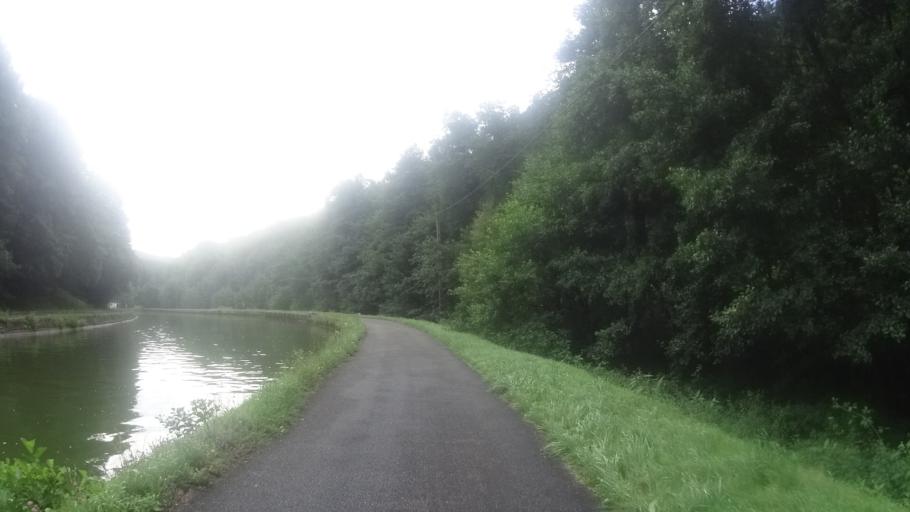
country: FR
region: Lorraine
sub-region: Departement de la Moselle
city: Phalsbourg
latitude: 48.7262
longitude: 7.2991
